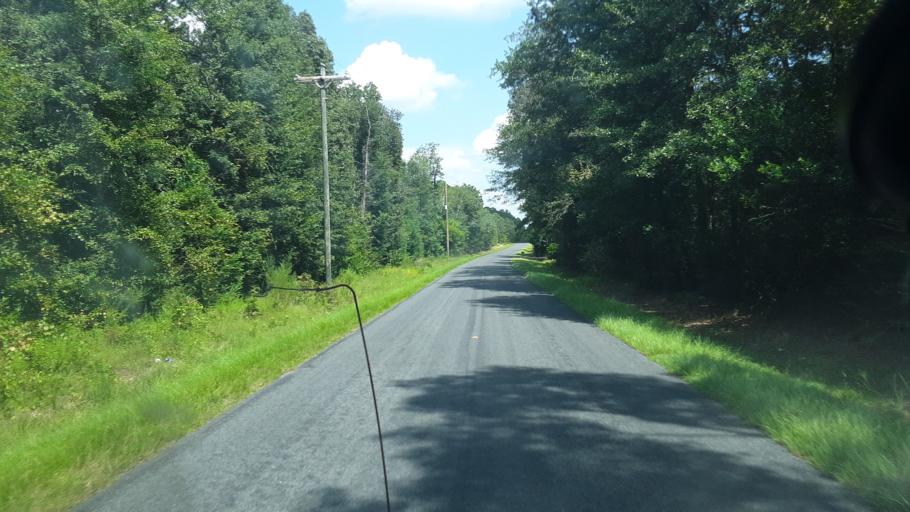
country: US
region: South Carolina
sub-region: Calhoun County
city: Oak Grove
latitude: 33.6984
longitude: -80.9620
